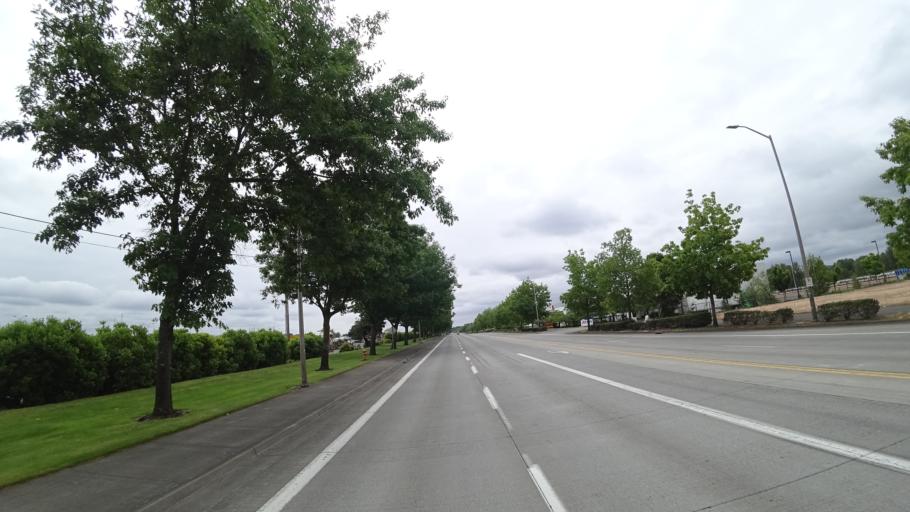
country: US
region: Washington
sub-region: Clark County
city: Lake Shore
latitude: 45.6300
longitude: -122.7446
